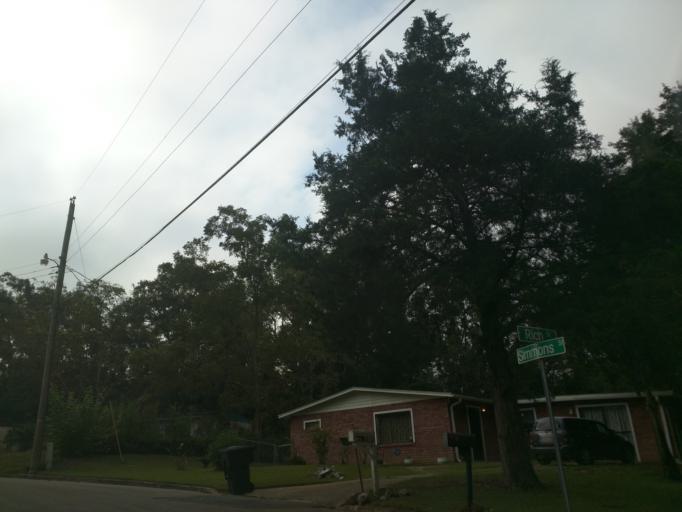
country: US
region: Florida
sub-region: Leon County
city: Tallahassee
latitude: 30.4606
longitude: -84.2934
